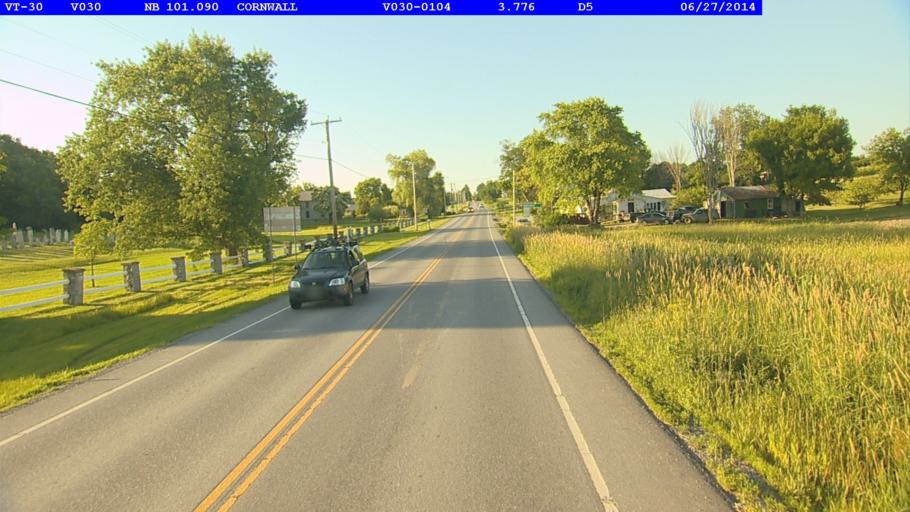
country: US
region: Vermont
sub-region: Addison County
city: Middlebury (village)
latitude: 43.9620
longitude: -73.2094
